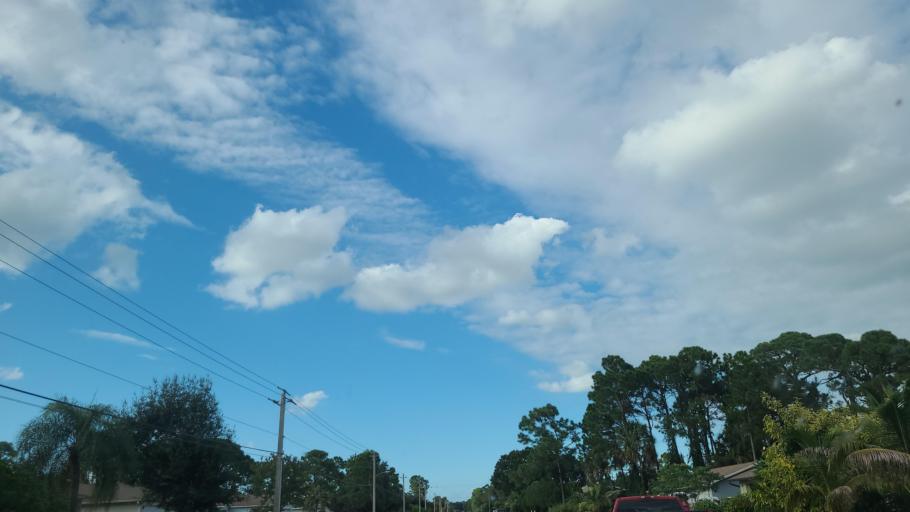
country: US
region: Florida
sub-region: Brevard County
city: West Melbourne
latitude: 28.0009
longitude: -80.6629
